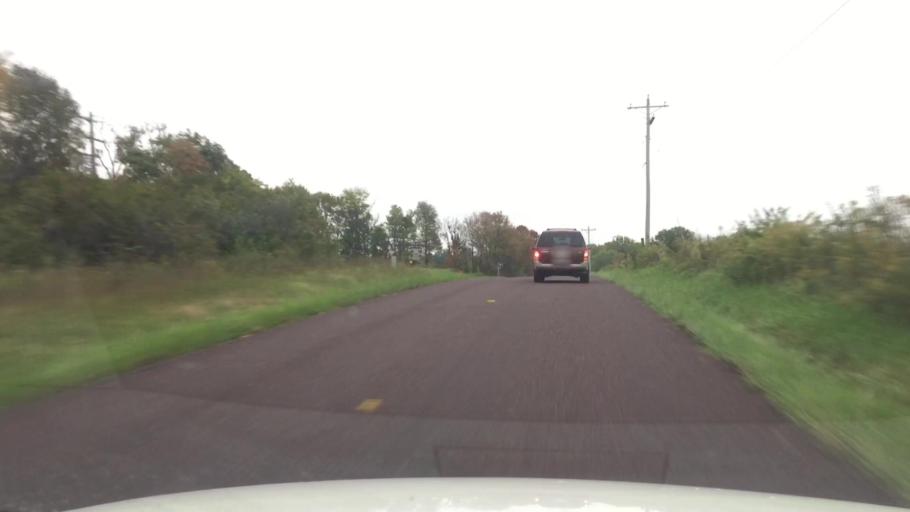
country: US
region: Missouri
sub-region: Boone County
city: Ashland
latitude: 38.8107
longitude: -92.2576
